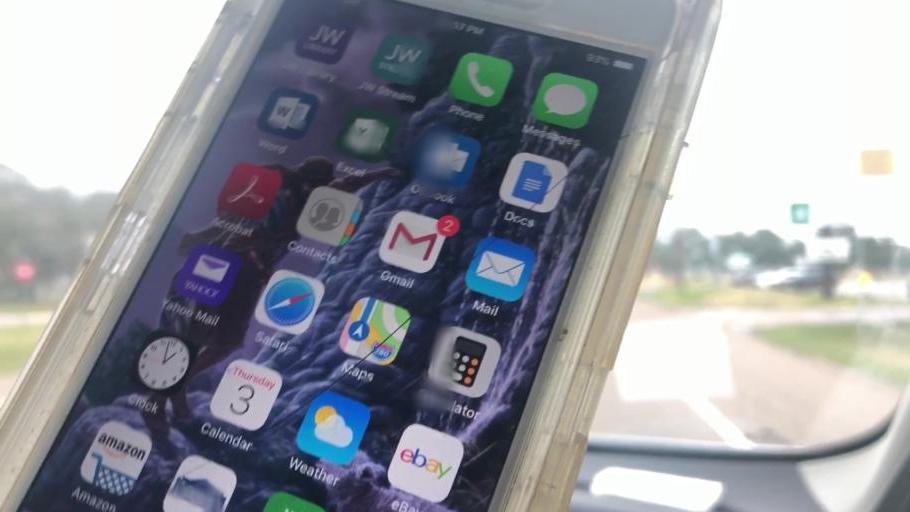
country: US
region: Texas
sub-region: Wharton County
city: Wharton
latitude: 29.3067
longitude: -96.0851
